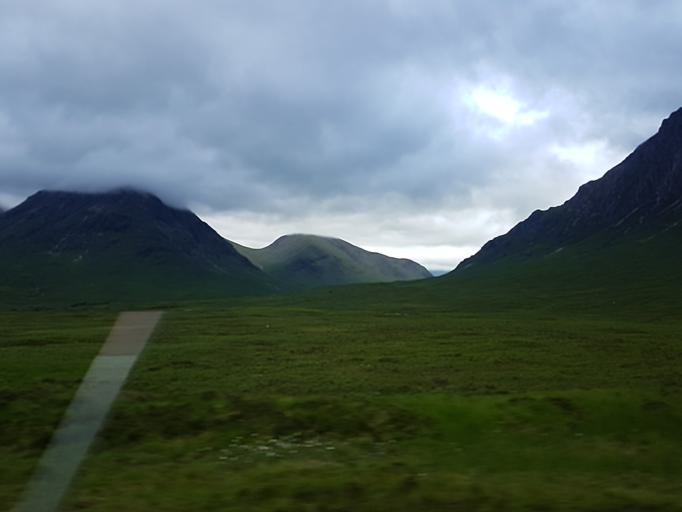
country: GB
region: Scotland
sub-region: Highland
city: Spean Bridge
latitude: 56.6554
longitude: -4.8665
